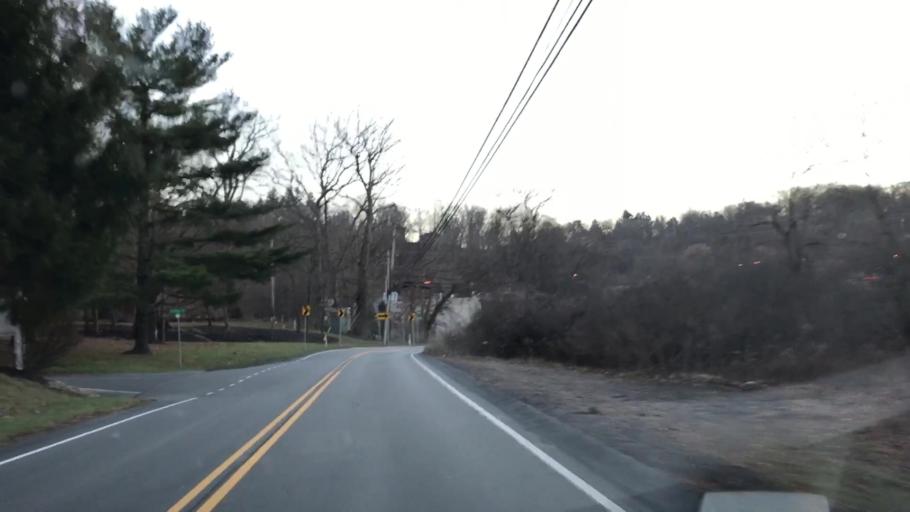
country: US
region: Pennsylvania
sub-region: Allegheny County
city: Franklin Park
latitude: 40.5877
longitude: -80.0367
